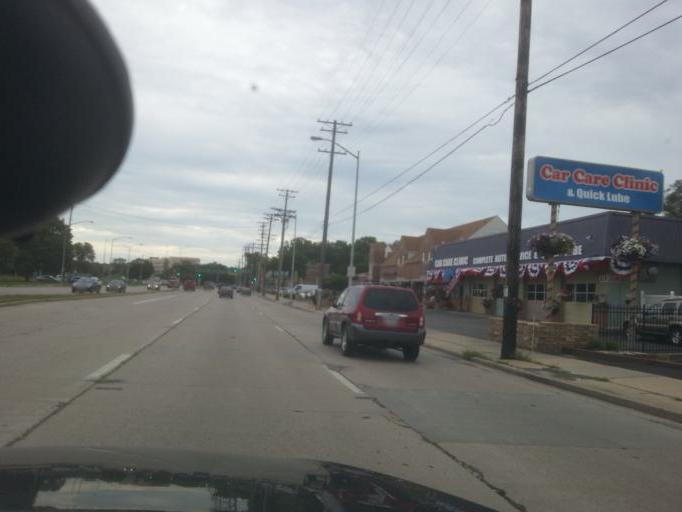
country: US
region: Wisconsin
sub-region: Dane County
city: Shorewood Hills
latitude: 43.0739
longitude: -89.4355
